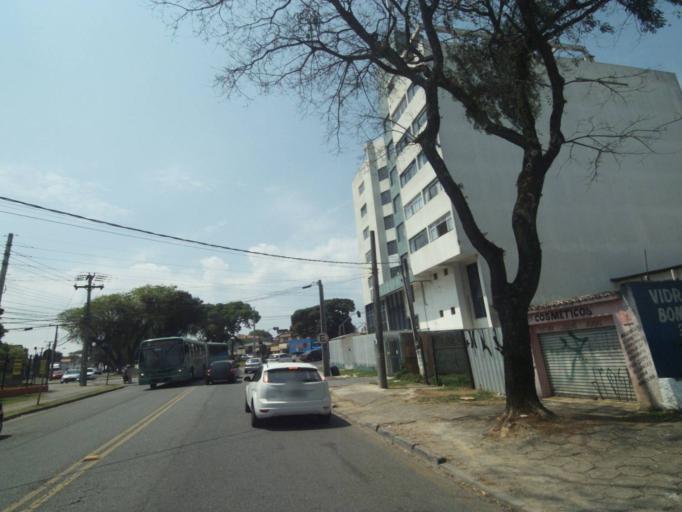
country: BR
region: Parana
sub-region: Curitiba
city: Curitiba
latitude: -25.4777
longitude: -49.3119
